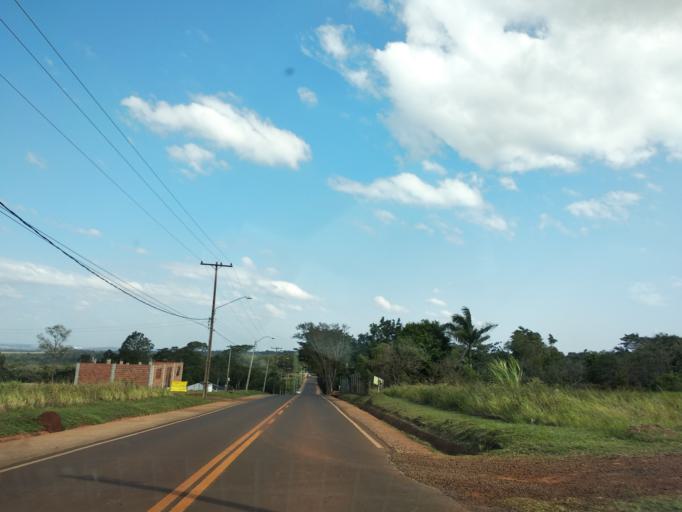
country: PY
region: Itapua
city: San Juan del Parana
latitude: -27.2916
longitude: -55.9572
